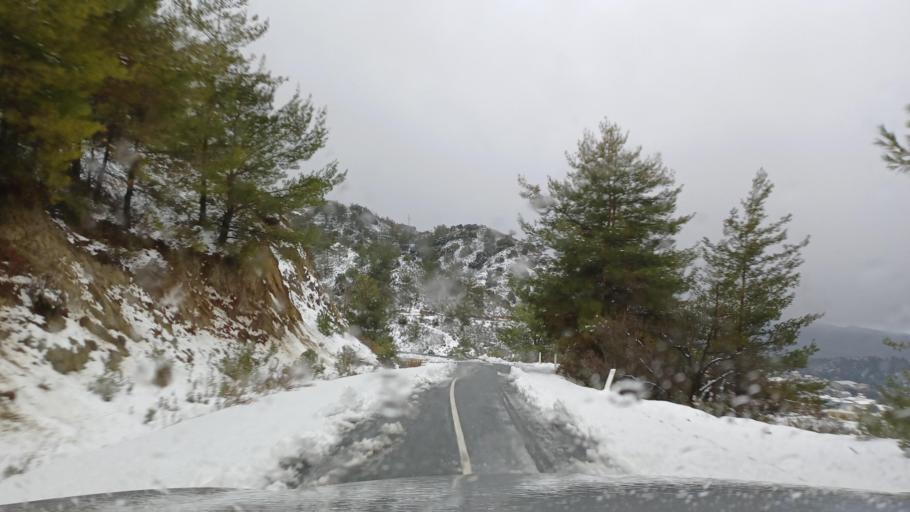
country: CY
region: Limassol
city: Pelendri
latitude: 34.9052
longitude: 32.9626
